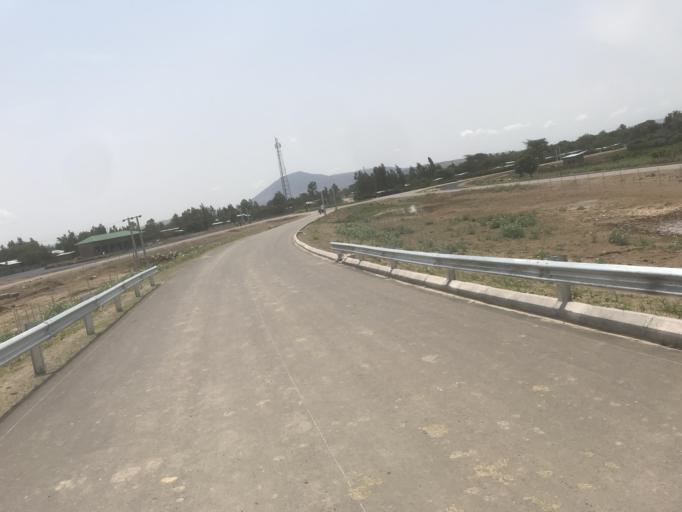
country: ET
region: Oromiya
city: Mojo
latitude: 8.3011
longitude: 38.9386
